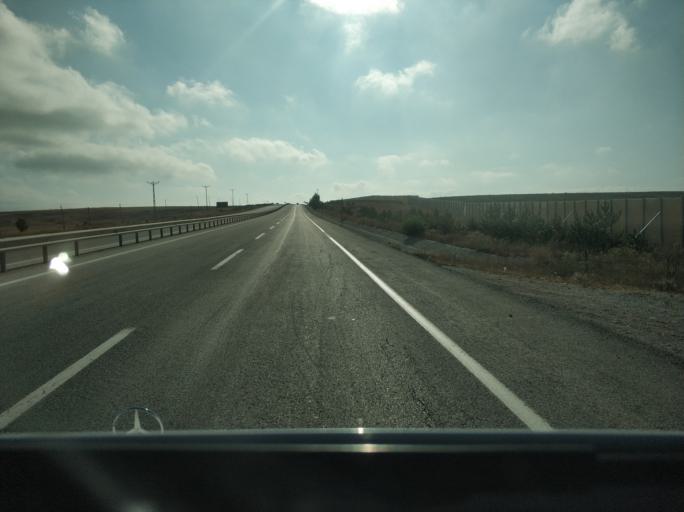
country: TR
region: Sivas
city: Yildizeli
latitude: 39.8351
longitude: 36.4043
